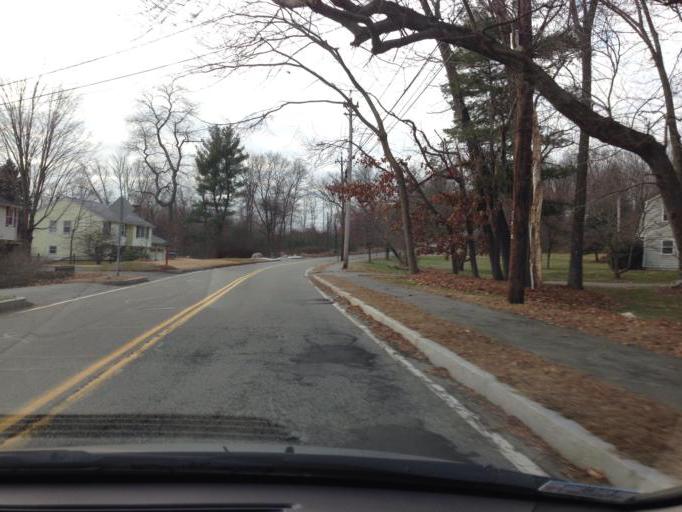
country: US
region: Massachusetts
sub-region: Middlesex County
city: Bedford
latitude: 42.4791
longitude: -71.2852
